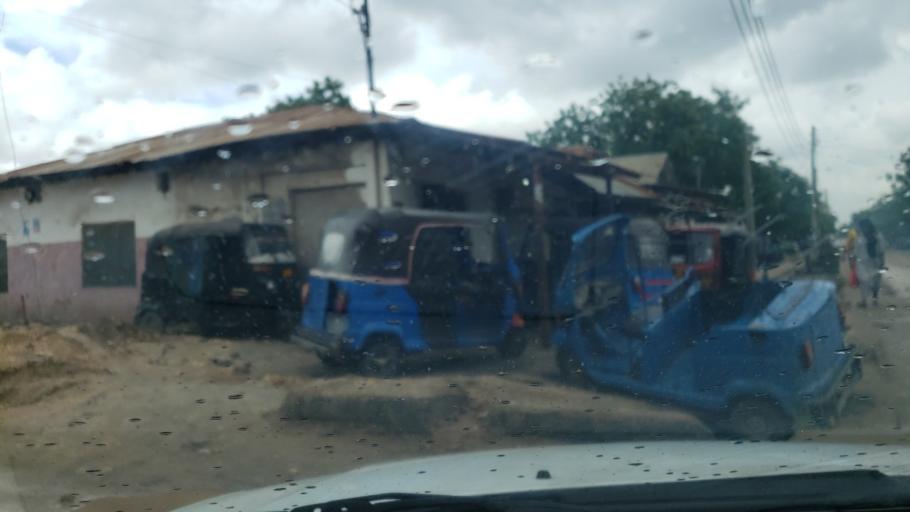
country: TZ
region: Dar es Salaam
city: Magomeni
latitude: -6.8108
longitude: 39.2572
